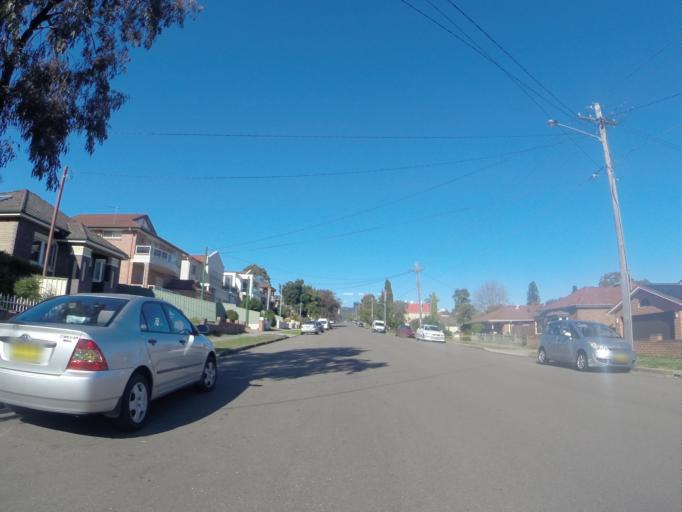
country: AU
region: New South Wales
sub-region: Hurstville
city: Penshurst
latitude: -33.9576
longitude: 151.0909
